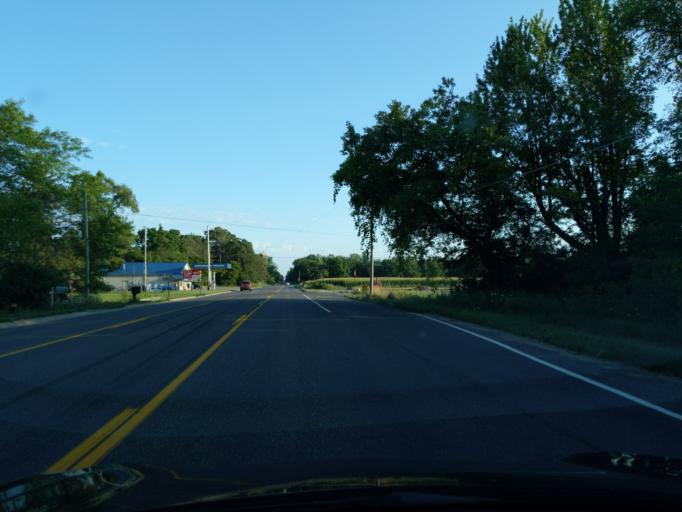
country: US
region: Michigan
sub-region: Midland County
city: Midland
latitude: 43.5683
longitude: -84.3696
